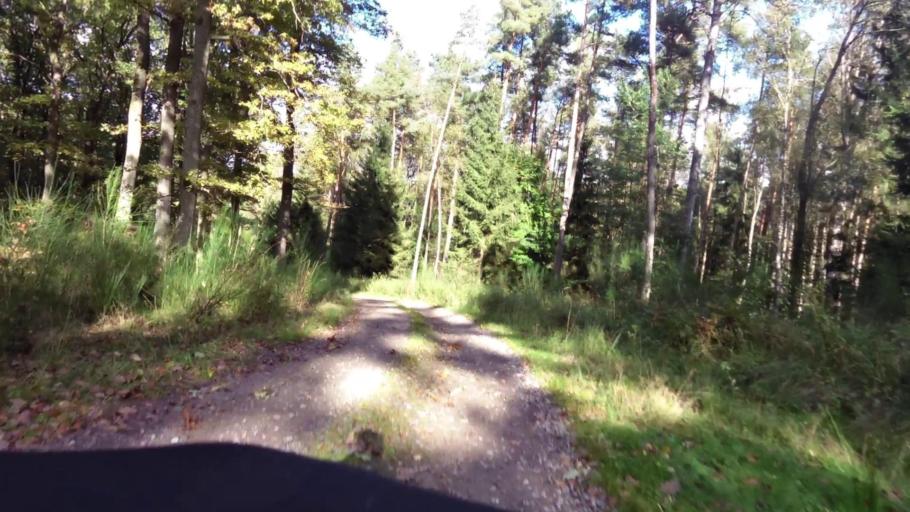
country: PL
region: West Pomeranian Voivodeship
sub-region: Powiat bialogardzki
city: Bialogard
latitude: 54.0403
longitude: 16.1359
